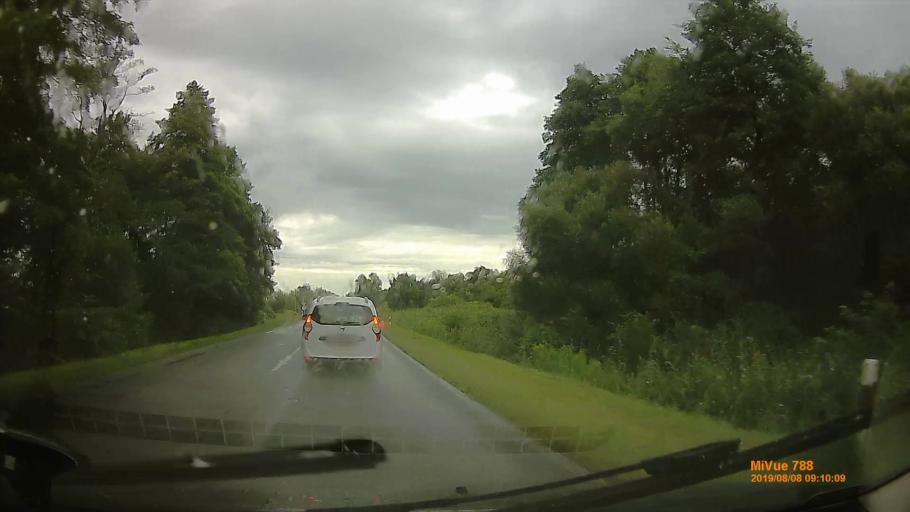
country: HU
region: Zala
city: Zalaegerszeg
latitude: 46.7669
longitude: 16.8577
